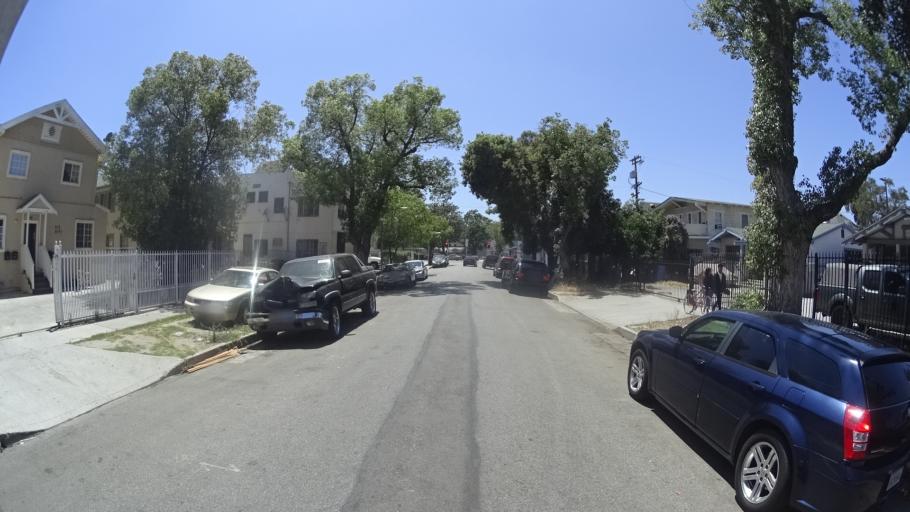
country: US
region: California
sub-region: Los Angeles County
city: View Park-Windsor Hills
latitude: 34.0091
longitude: -118.2905
